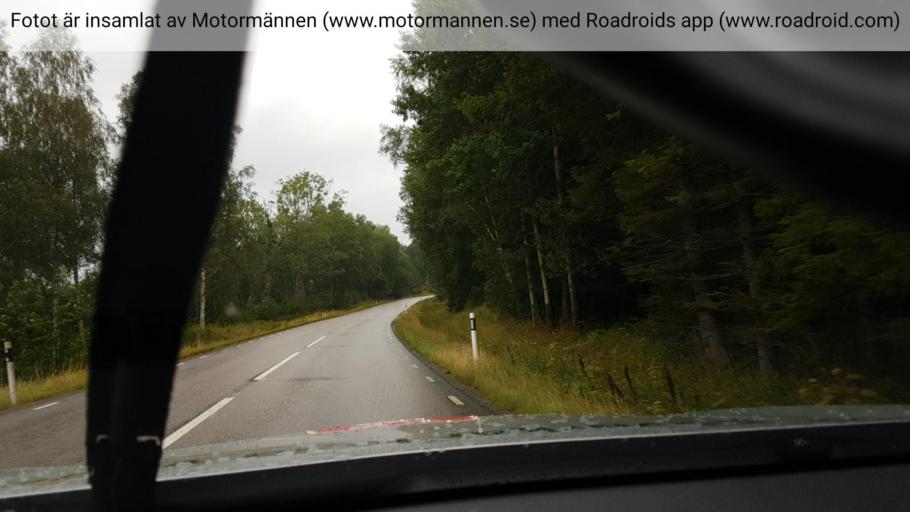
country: SE
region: Vaestra Goetaland
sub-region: Bengtsfors Kommun
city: Dals Langed
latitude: 58.9028
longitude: 12.2186
